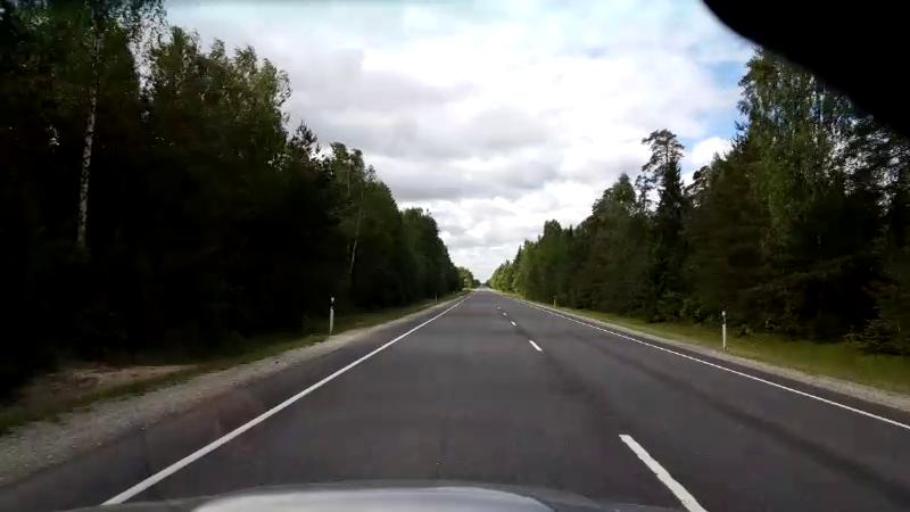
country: EE
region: Raplamaa
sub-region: Maerjamaa vald
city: Marjamaa
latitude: 58.8727
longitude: 24.4436
